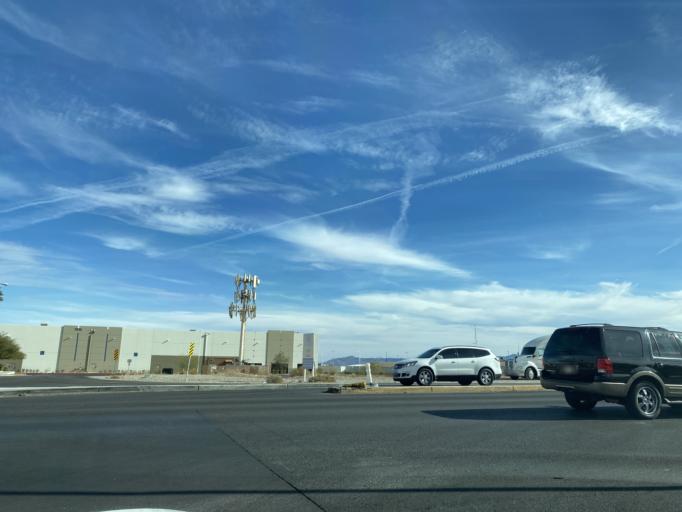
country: US
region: Nevada
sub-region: Clark County
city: Enterprise
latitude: 36.0601
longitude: -115.2250
